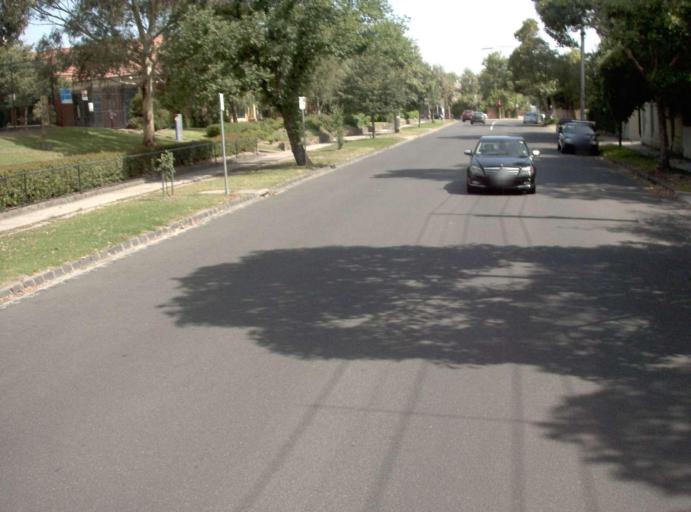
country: AU
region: Victoria
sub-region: Boroondara
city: Hawthorn East
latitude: -37.8145
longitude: 145.0467
